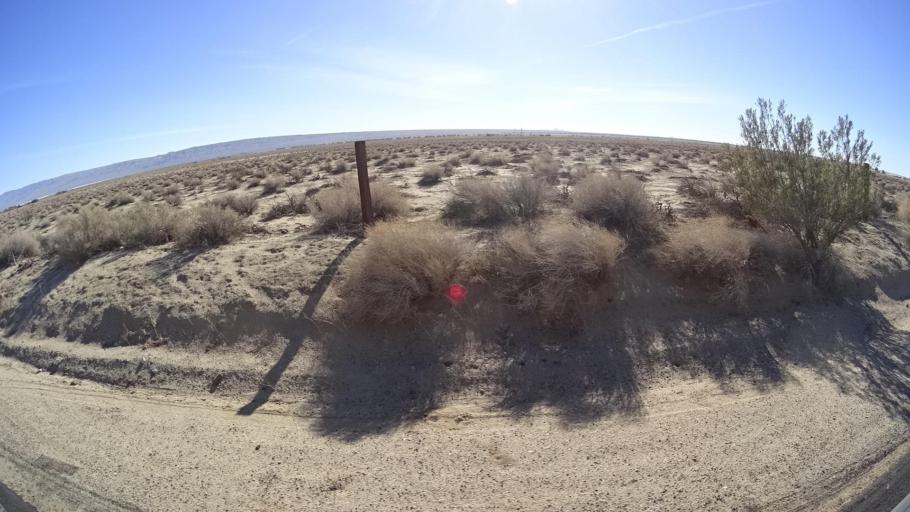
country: US
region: California
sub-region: Kern County
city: California City
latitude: 35.3023
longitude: -117.9788
